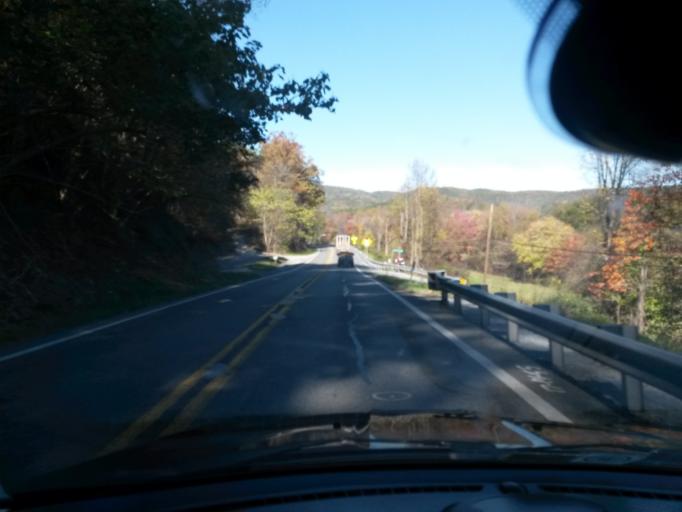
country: US
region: Virginia
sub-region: Alleghany County
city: Clifton Forge
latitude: 37.7835
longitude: -79.7795
